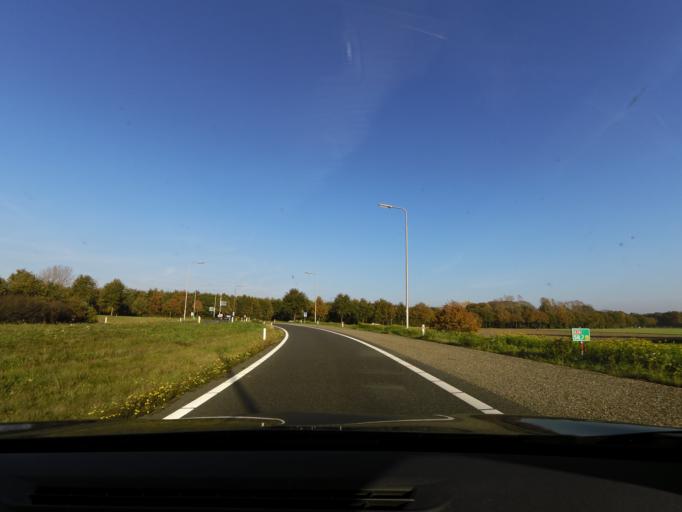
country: NL
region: North Brabant
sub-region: Gemeente Breda
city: Breda
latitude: 51.5354
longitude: 4.7996
